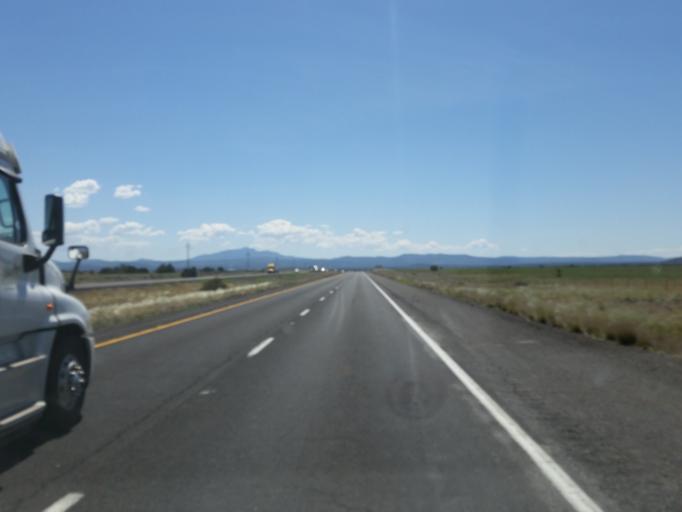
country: US
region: Arizona
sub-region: Yavapai County
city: Paulden
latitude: 35.2248
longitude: -112.5629
